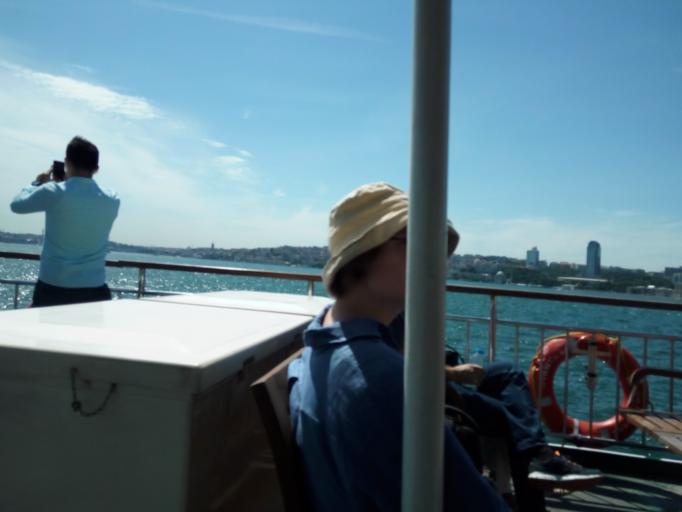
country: TR
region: Istanbul
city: UEskuedar
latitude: 41.0324
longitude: 29.0139
